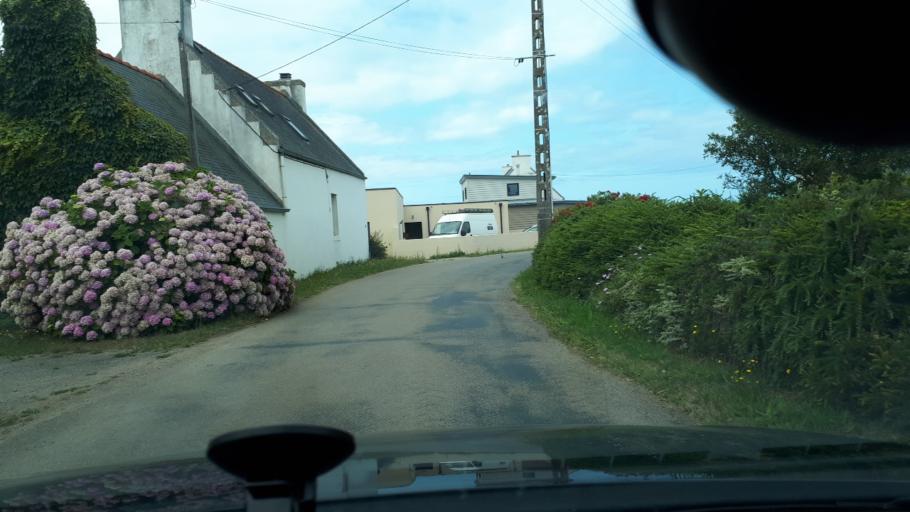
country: FR
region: Brittany
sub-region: Departement du Finistere
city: Pouldreuzic
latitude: 47.9589
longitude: -4.3944
